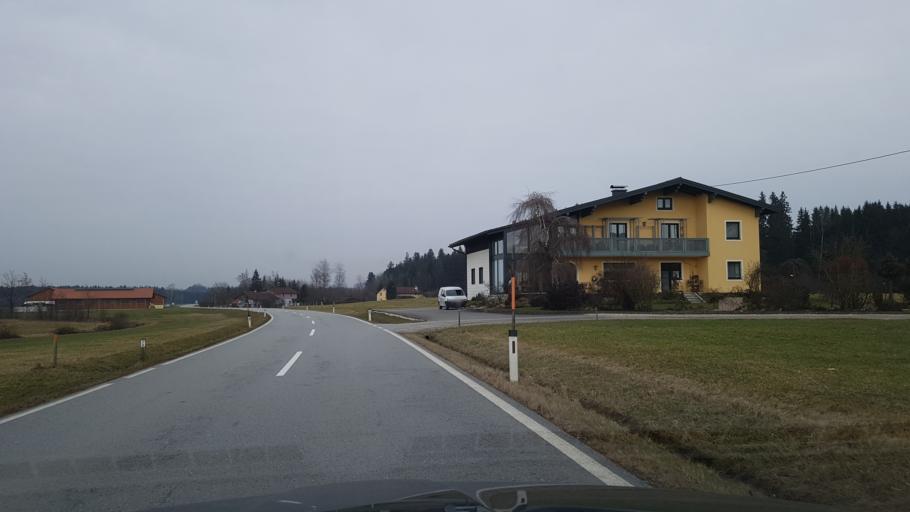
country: AT
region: Salzburg
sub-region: Politischer Bezirk Salzburg-Umgebung
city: Lamprechtshausen
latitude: 48.0360
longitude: 12.9510
